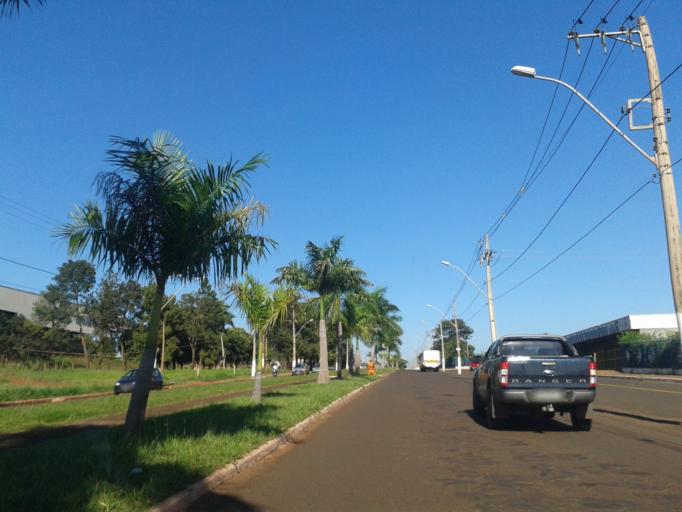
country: BR
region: Minas Gerais
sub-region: Ituiutaba
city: Ituiutaba
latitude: -18.9722
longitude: -49.4800
